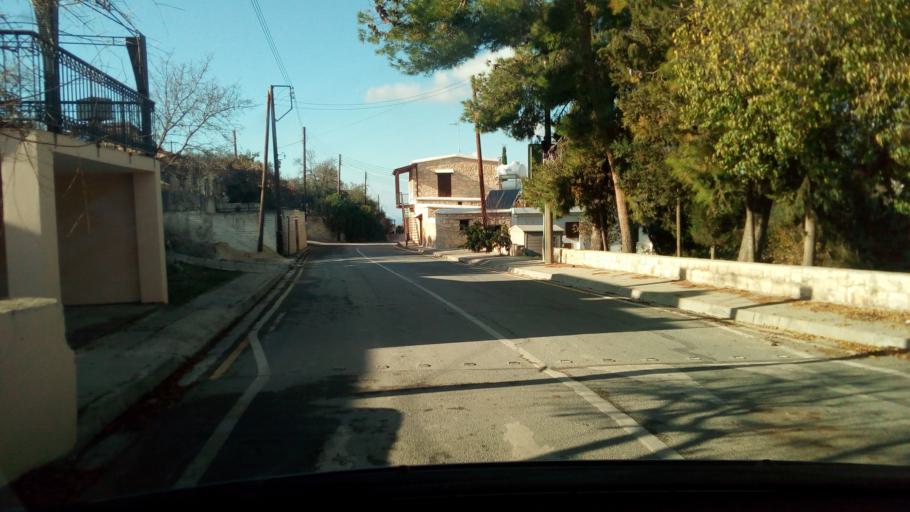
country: CY
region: Pafos
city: Polis
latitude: 34.9416
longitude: 32.5042
